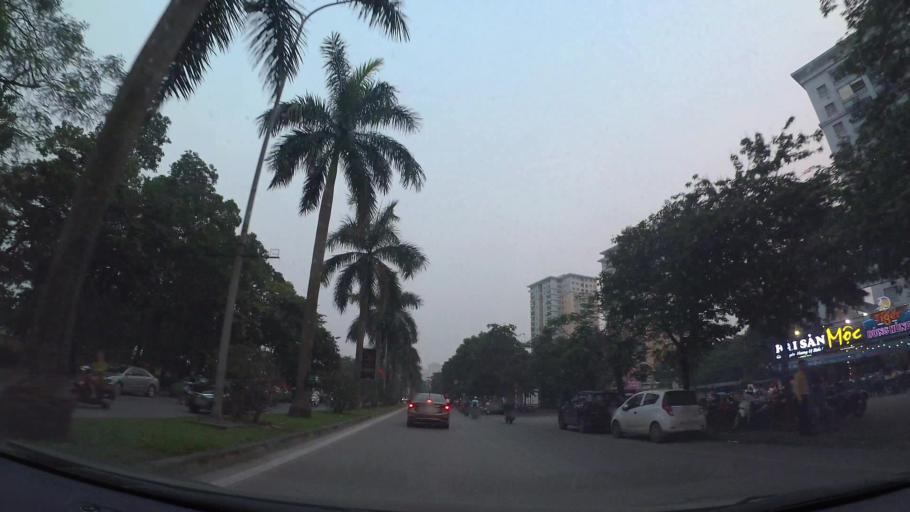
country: VN
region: Ha Noi
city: Ha Dong
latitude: 20.9742
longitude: 105.7898
